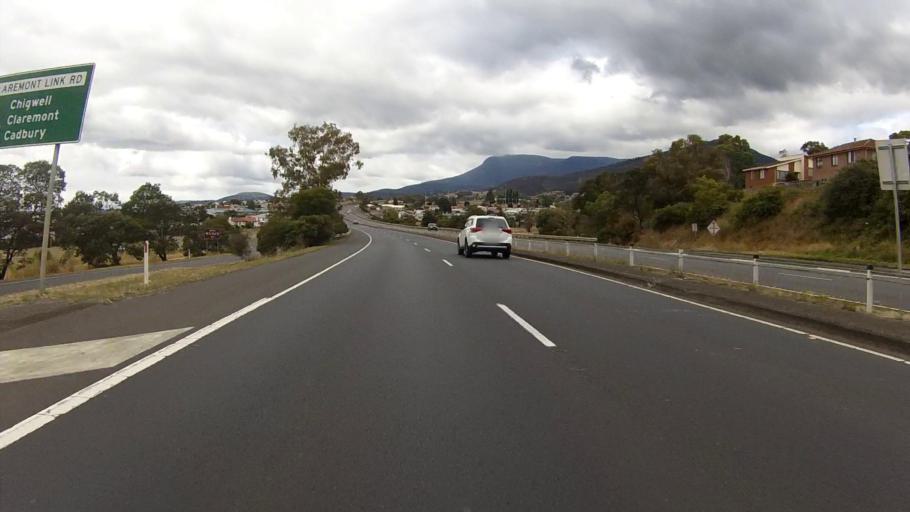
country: AU
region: Tasmania
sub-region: Glenorchy
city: Claremont
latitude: -42.7978
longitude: 147.2484
